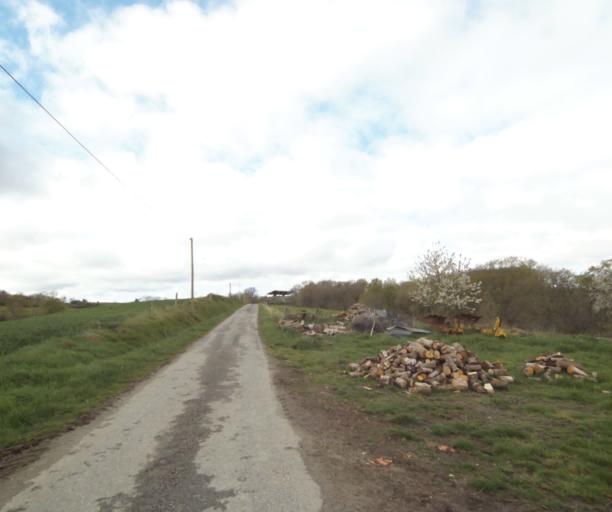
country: FR
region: Midi-Pyrenees
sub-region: Departement de l'Ariege
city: Saverdun
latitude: 43.2195
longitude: 1.5419
